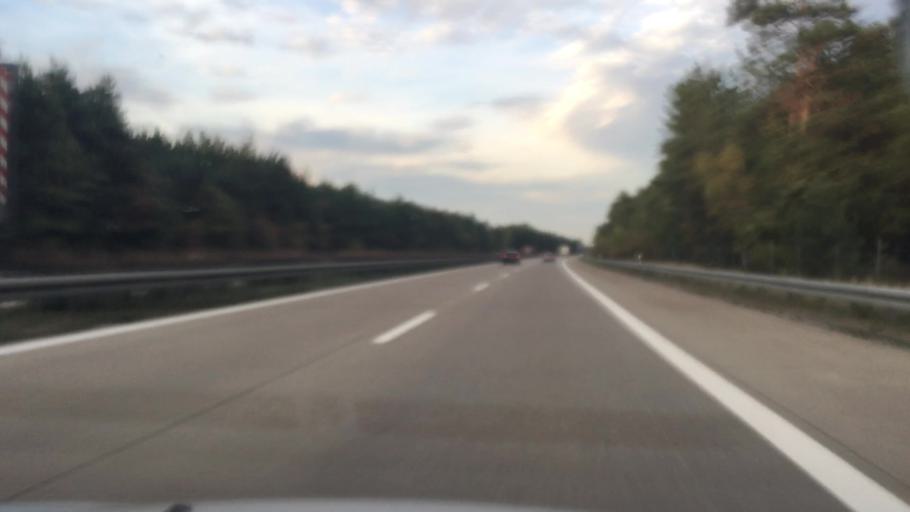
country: DE
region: Brandenburg
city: Ruhland
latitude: 51.4467
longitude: 13.8400
